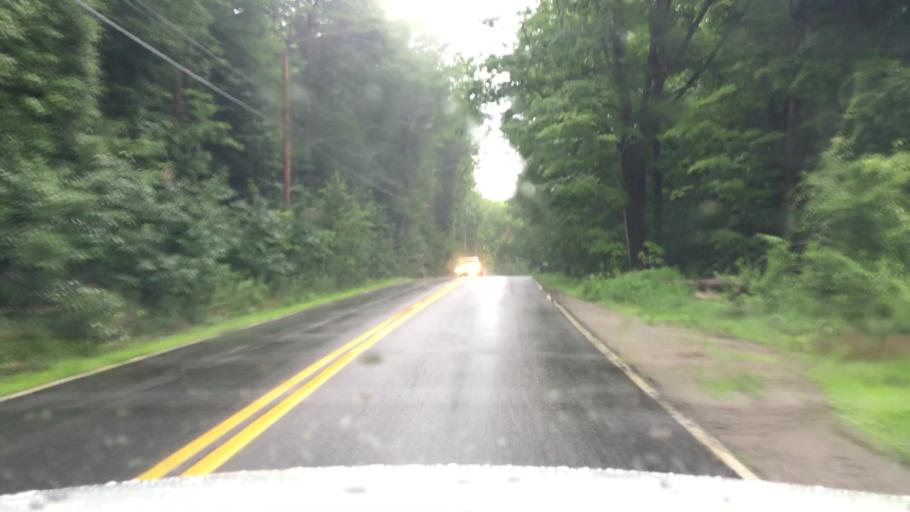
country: US
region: Maine
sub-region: Kennebec County
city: Winthrop
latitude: 44.2981
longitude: -69.9267
